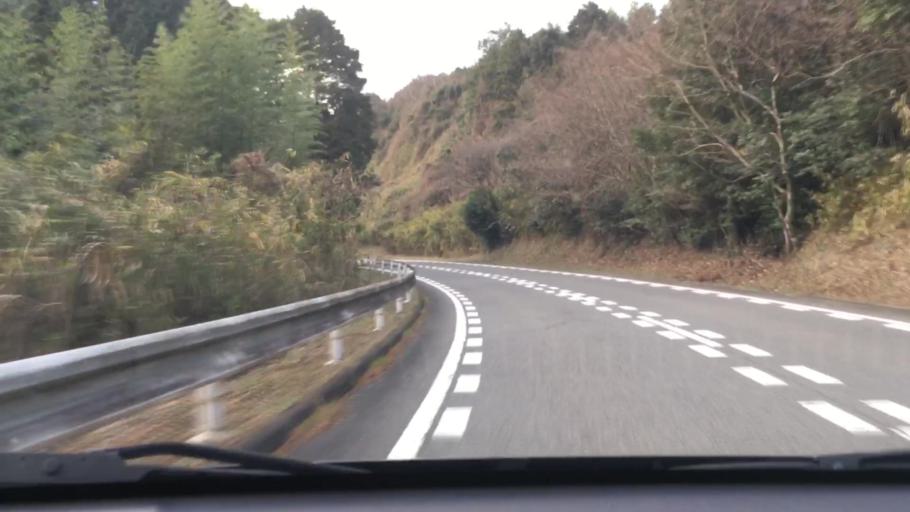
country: JP
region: Oita
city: Hiji
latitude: 33.4131
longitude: 131.4235
